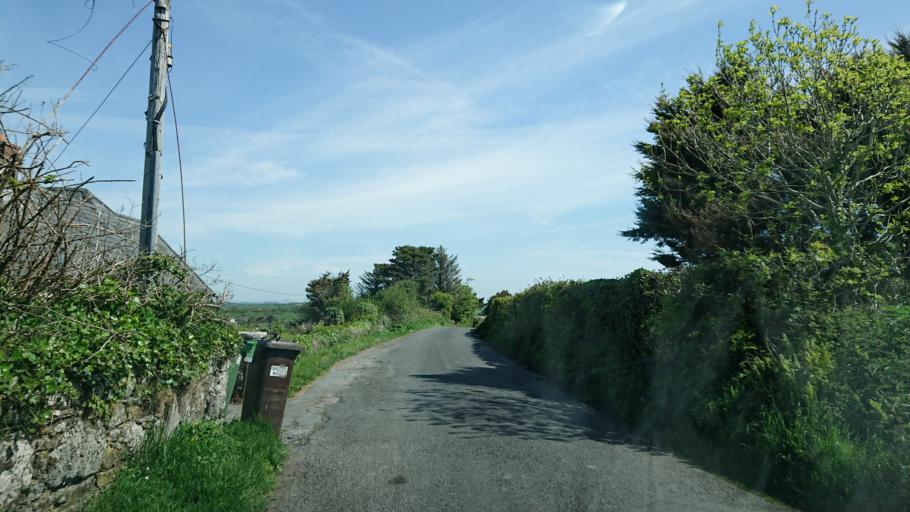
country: IE
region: Munster
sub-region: Waterford
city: Tra Mhor
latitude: 52.1523
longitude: -7.0748
